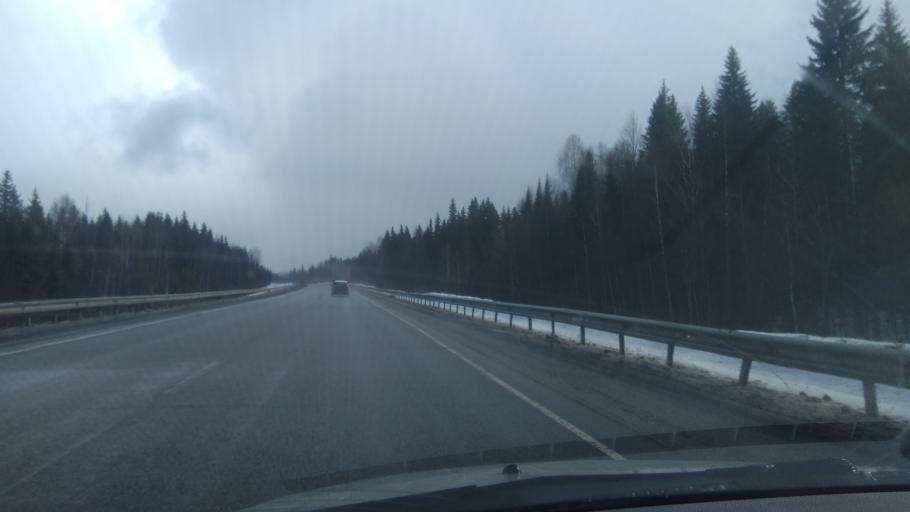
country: RU
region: Sverdlovsk
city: Arti
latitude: 56.7880
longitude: 58.5091
